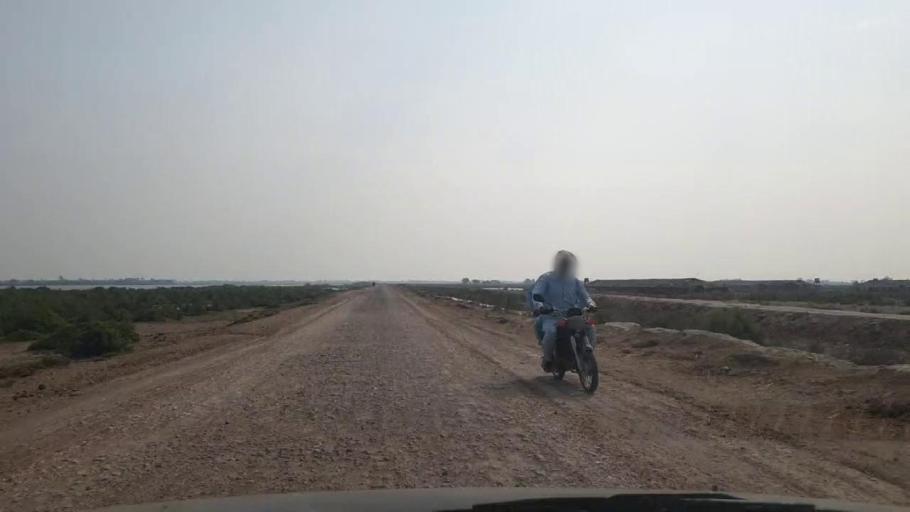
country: PK
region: Sindh
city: Tando Muhammad Khan
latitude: 25.0890
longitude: 68.3846
